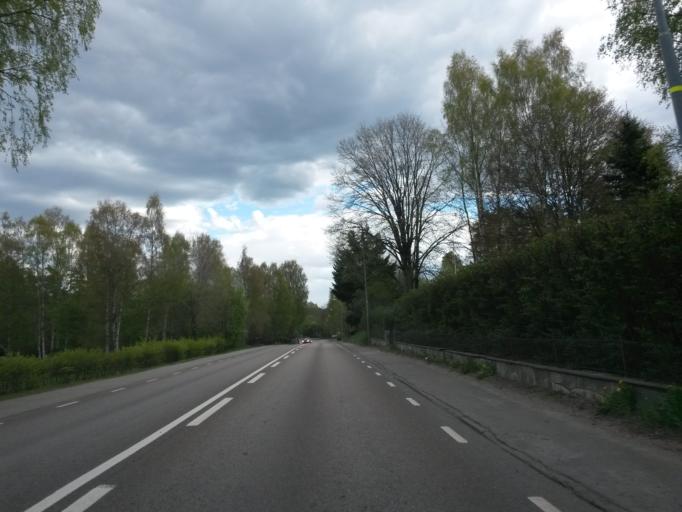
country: SE
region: Vaestra Goetaland
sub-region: Boras Kommun
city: Boras
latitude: 57.8295
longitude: 12.9956
